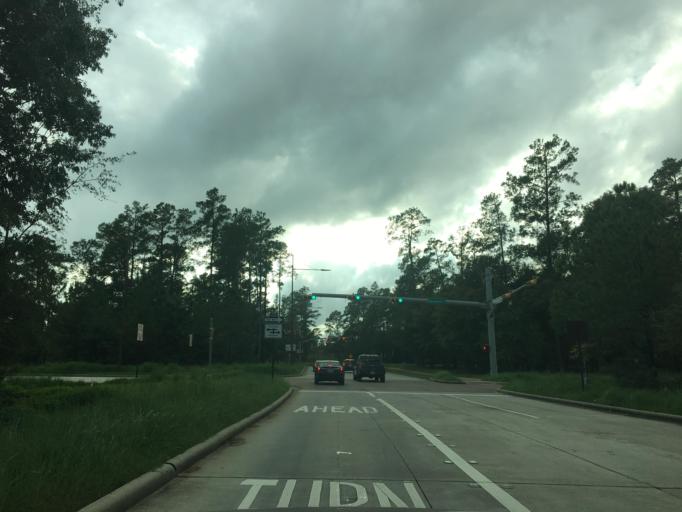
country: US
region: Texas
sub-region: Harris County
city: Spring
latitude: 30.0971
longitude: -95.4506
